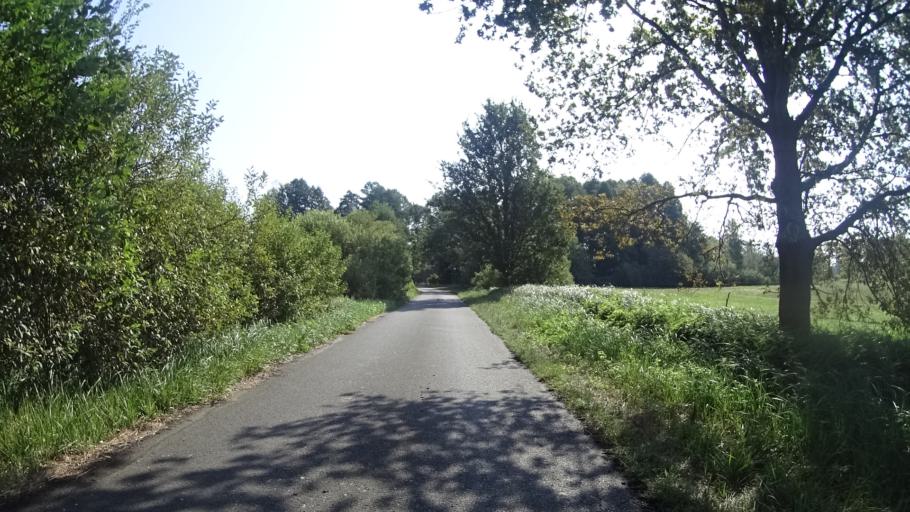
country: DE
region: Brandenburg
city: Straupitz
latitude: 51.8950
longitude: 14.1235
